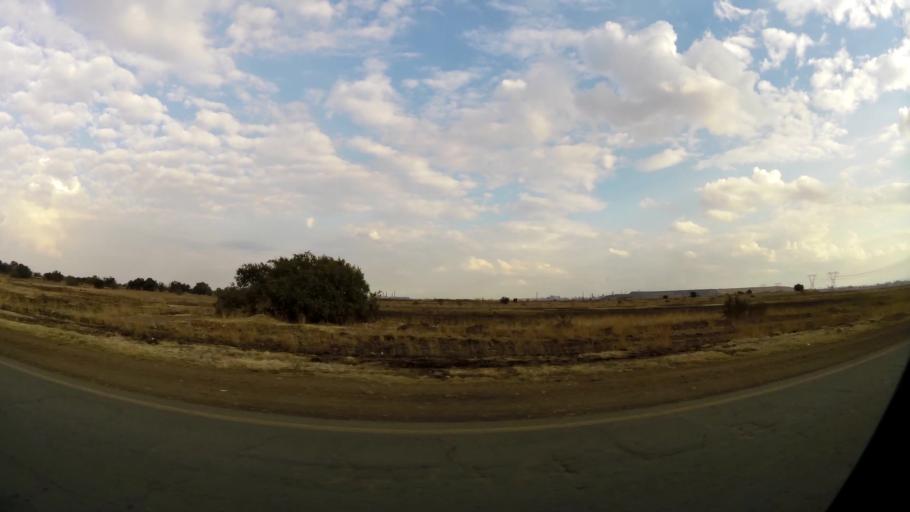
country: ZA
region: Gauteng
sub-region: Sedibeng District Municipality
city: Vanderbijlpark
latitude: -26.6190
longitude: 27.8308
